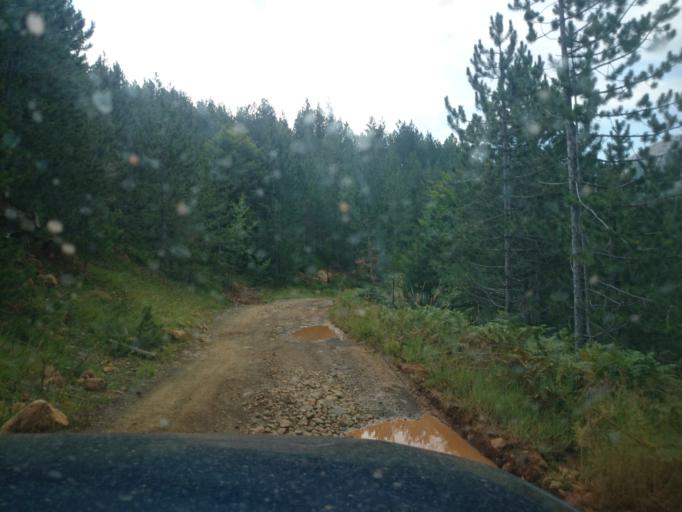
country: AL
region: Diber
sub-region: Rrethi i Dibres
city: Fushe-Lure
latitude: 41.7991
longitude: 20.1575
